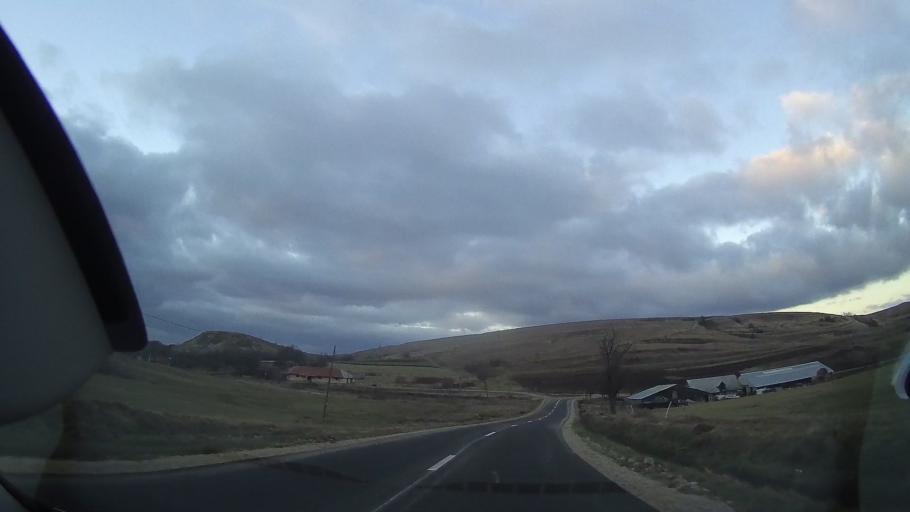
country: RO
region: Cluj
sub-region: Comuna Izvoru Crisului
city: Izvoru Crisului
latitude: 46.8023
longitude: 23.1099
